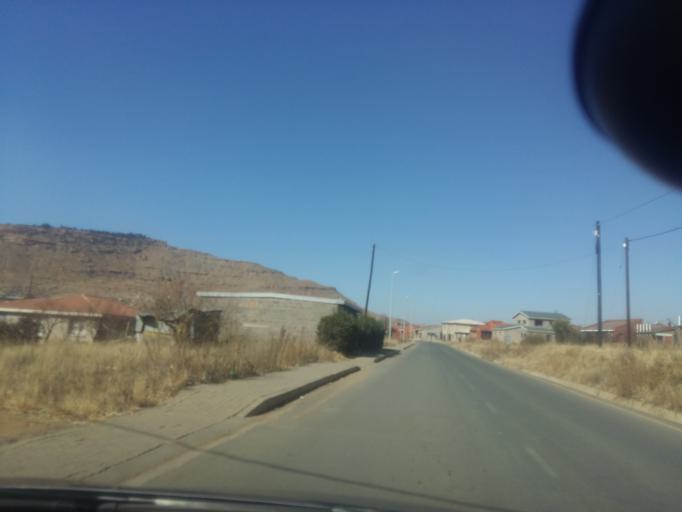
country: LS
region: Maseru
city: Maseru
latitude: -29.3421
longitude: 27.4546
